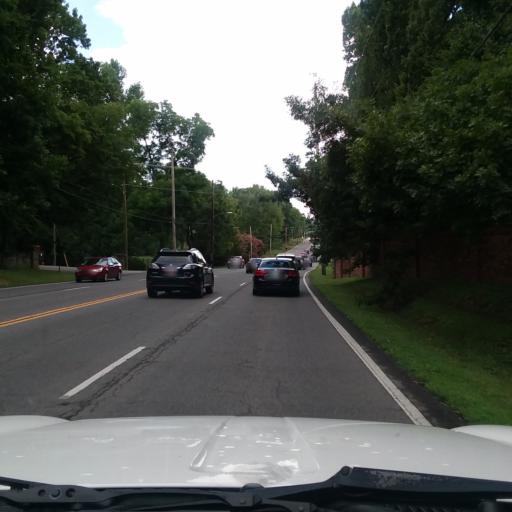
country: US
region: Tennessee
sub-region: Davidson County
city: Oak Hill
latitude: 36.0919
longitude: -86.7715
